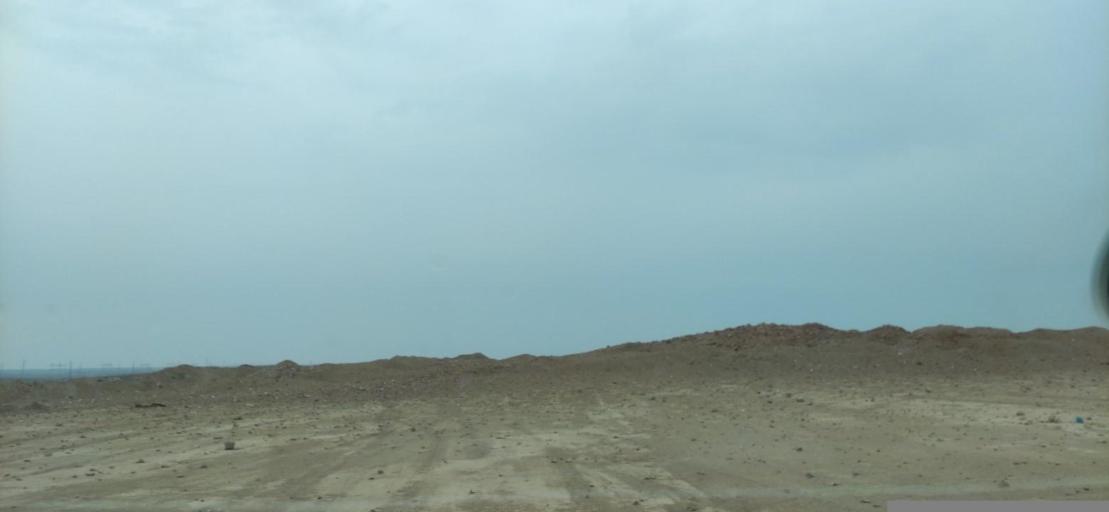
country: KZ
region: Qaraghandy
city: Saryshaghan
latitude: 46.1242
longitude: 73.5960
